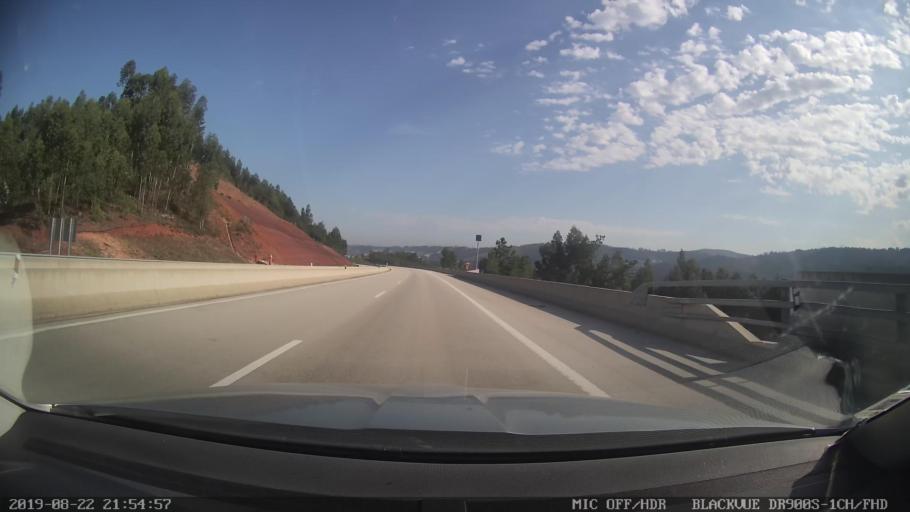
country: PT
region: Coimbra
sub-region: Coimbra
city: Coimbra
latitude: 40.1444
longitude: -8.3832
